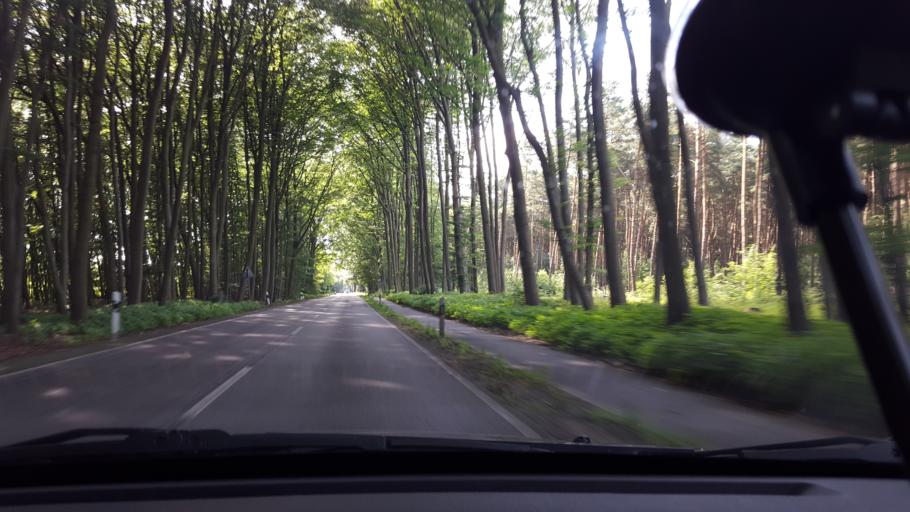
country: DE
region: North Rhine-Westphalia
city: Marl
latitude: 51.6592
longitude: 7.0465
